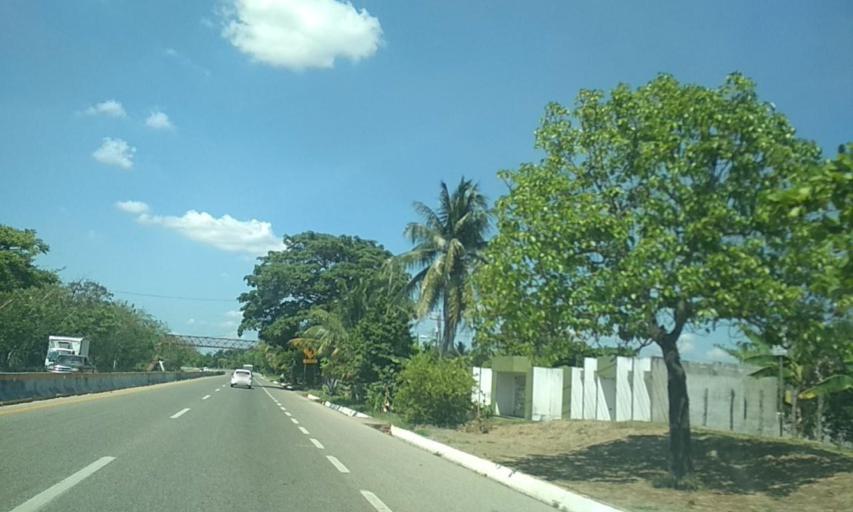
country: MX
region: Tabasco
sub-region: Huimanguillo
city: El Dorado
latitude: 17.8827
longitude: -93.3690
